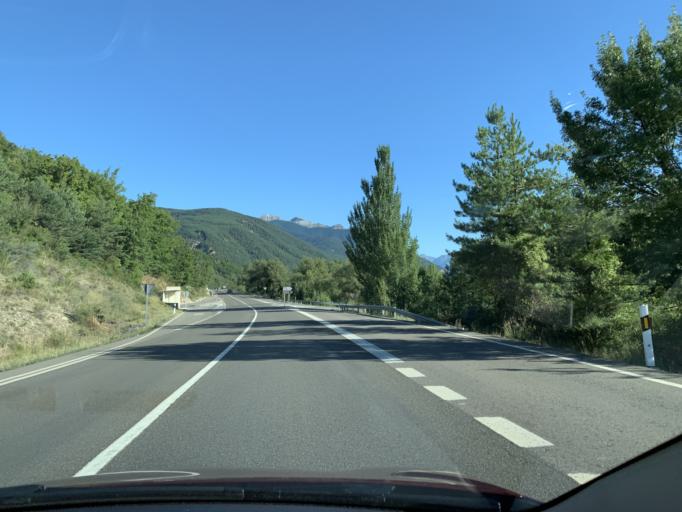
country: ES
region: Aragon
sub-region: Provincia de Huesca
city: Biescas
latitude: 42.5778
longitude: -0.3245
